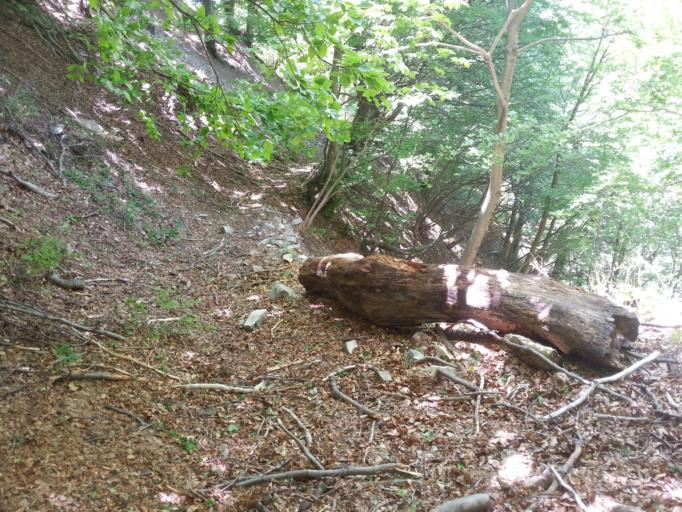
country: IT
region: Lombardy
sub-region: Provincia di Como
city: Bene Lario
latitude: 46.0031
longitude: 9.1643
